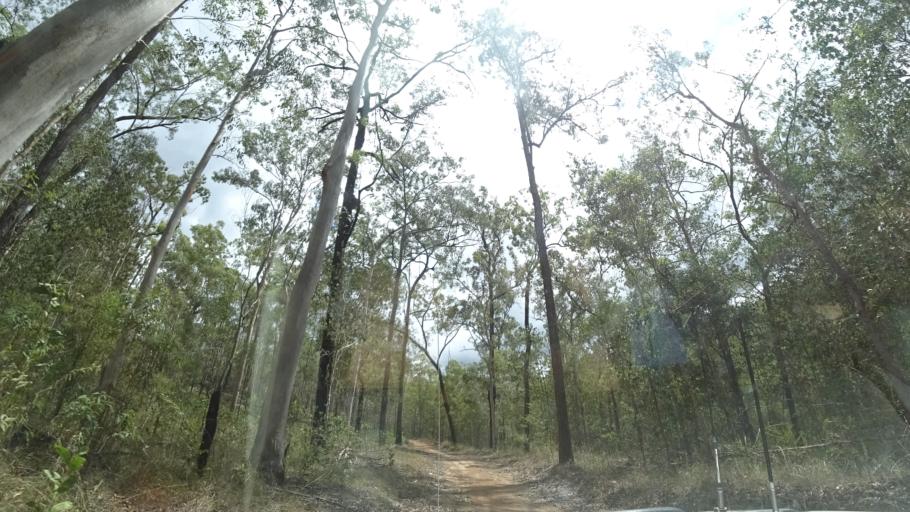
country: AU
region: Queensland
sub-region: Moreton Bay
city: Highvale
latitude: -27.4341
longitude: 152.7524
